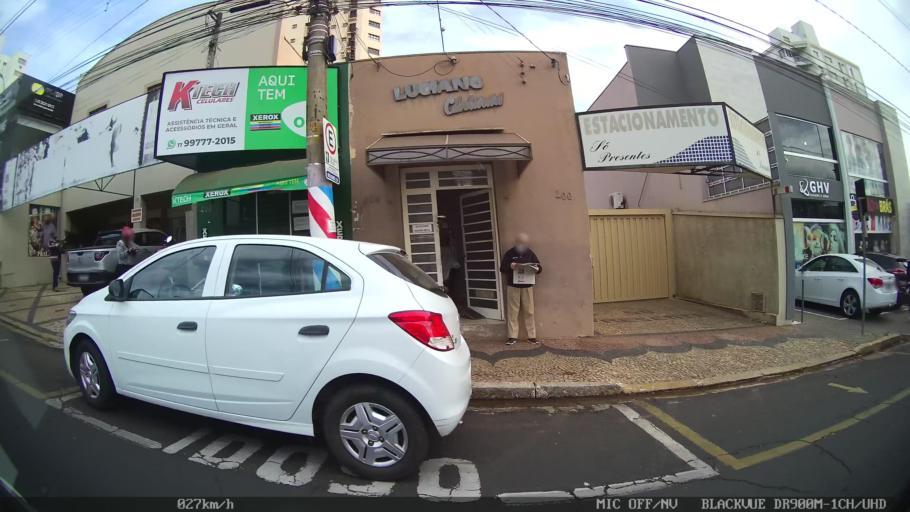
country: BR
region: Sao Paulo
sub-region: Catanduva
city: Catanduva
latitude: -21.1345
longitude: -48.9728
